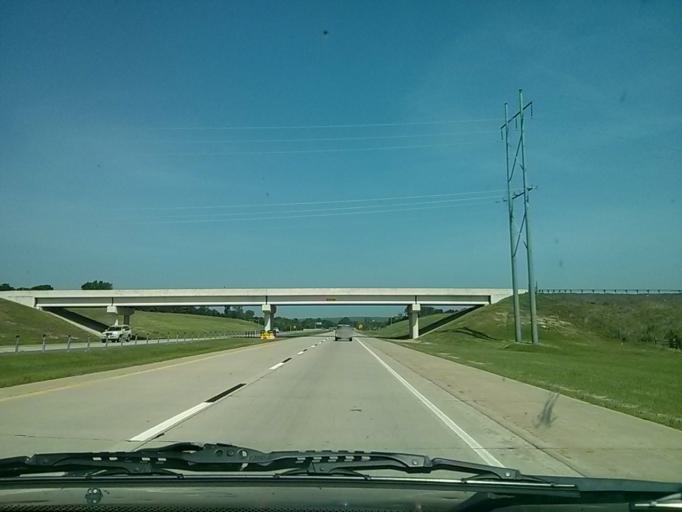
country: US
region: Oklahoma
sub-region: Creek County
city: Sapulpa
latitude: 36.0180
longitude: -96.0649
